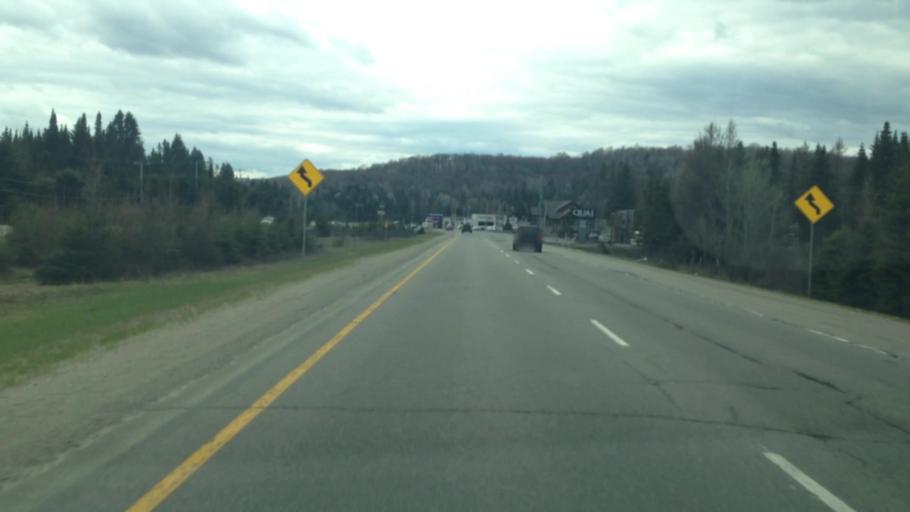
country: CA
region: Quebec
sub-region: Laurentides
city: Sainte-Agathe-des-Monts
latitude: 46.0739
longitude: -74.3149
